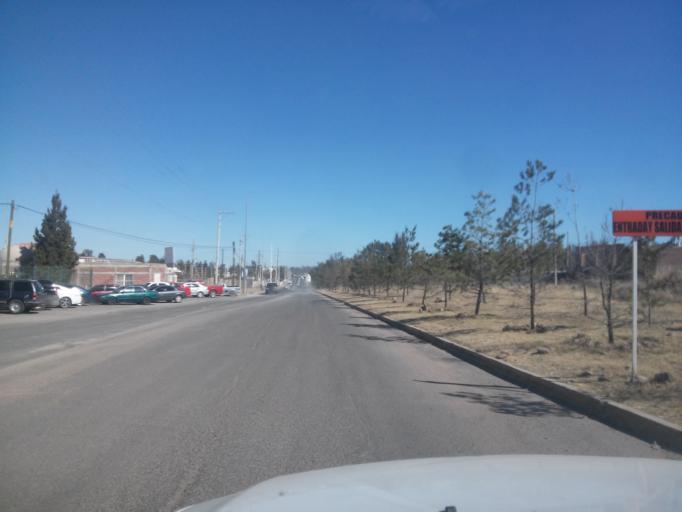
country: MX
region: Durango
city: Victoria de Durango
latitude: 24.0206
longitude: -104.7031
